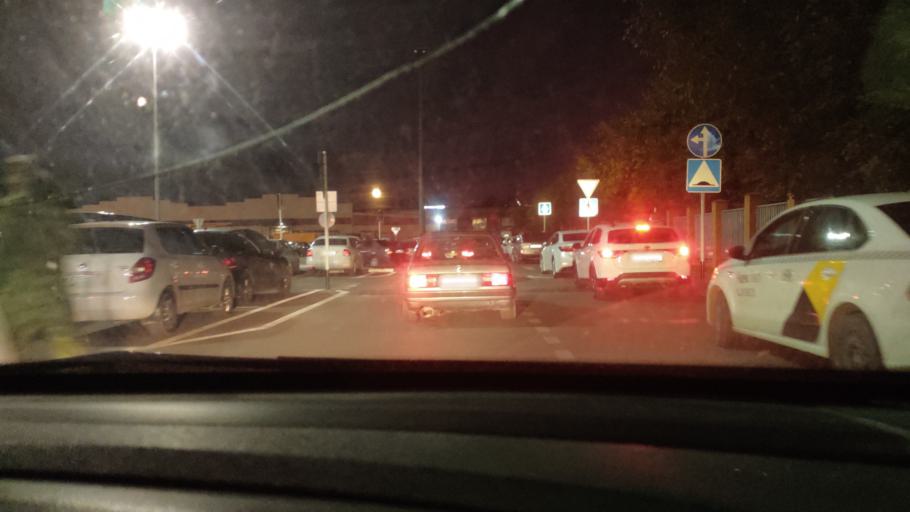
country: RU
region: Krasnodarskiy
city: Krasnodar
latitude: 45.1016
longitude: 38.9881
